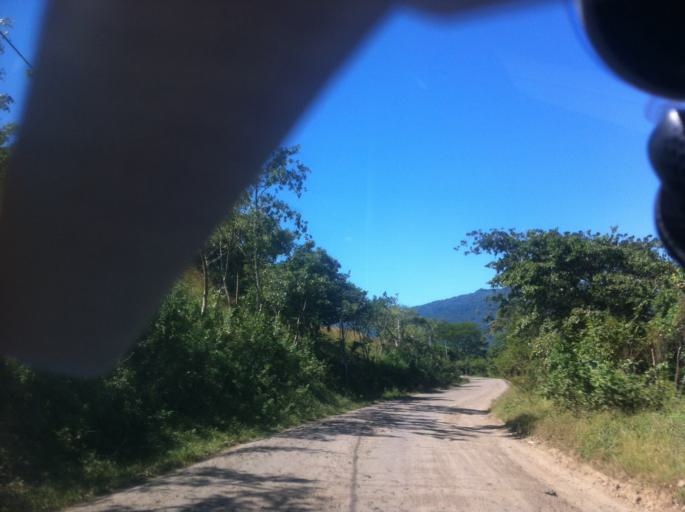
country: NI
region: Matagalpa
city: San Ramon
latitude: 12.8561
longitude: -85.8438
